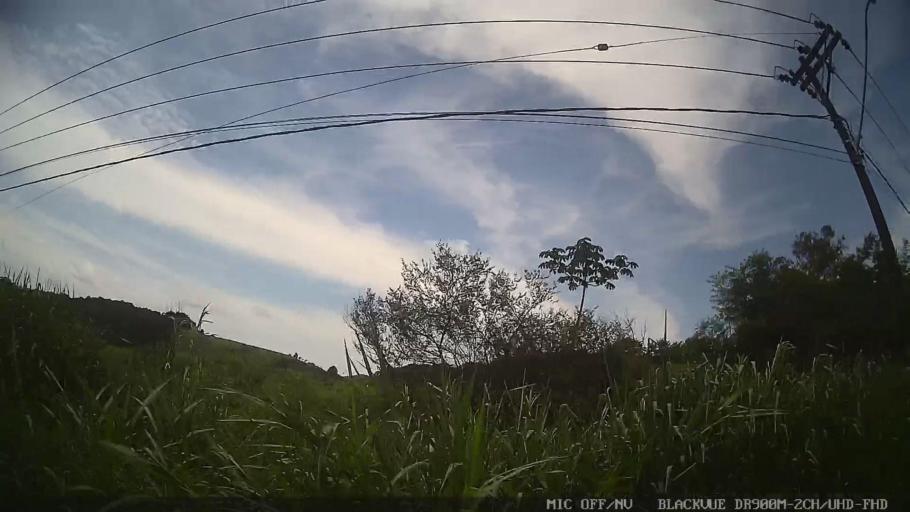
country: BR
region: Sao Paulo
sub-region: Aruja
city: Aruja
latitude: -23.4311
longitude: -46.2535
